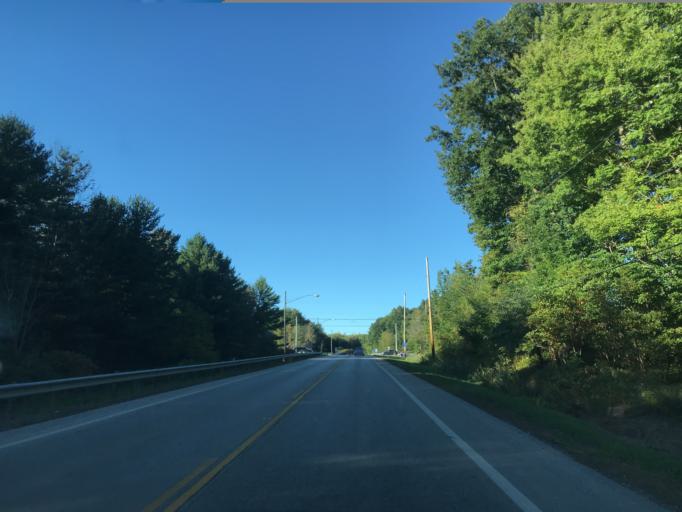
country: US
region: Ohio
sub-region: Ashtabula County
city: Geneva
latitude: 41.7584
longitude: -80.9410
